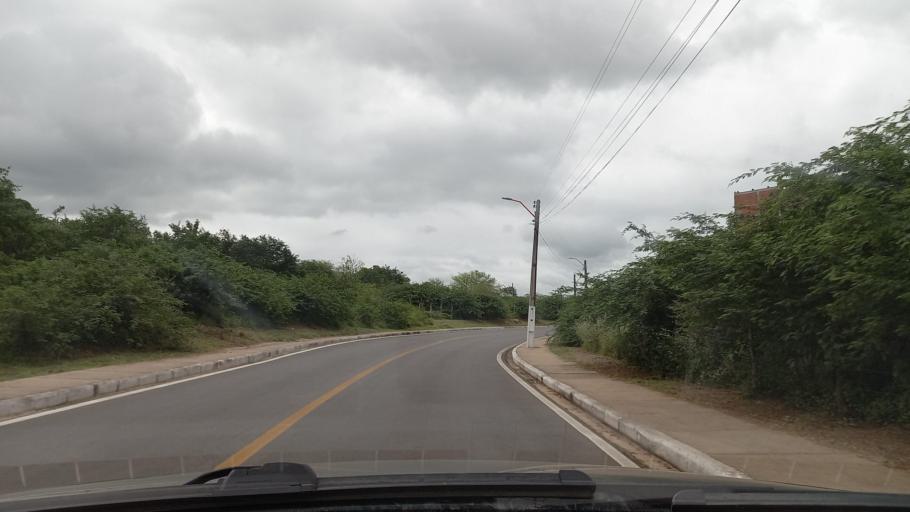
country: BR
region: Sergipe
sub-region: Caninde De Sao Francisco
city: Caninde de Sao Francisco
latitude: -9.6161
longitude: -37.7645
